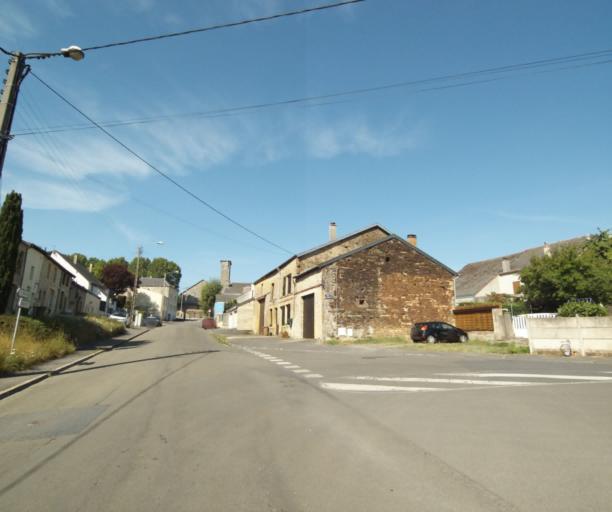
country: FR
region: Champagne-Ardenne
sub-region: Departement des Ardennes
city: Warcq
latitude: 49.7871
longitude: 4.6934
